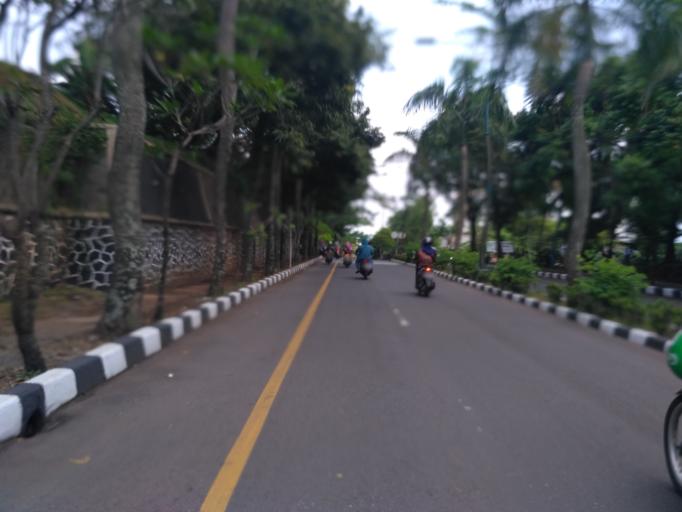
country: ID
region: Central Java
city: Semarang
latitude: -7.0531
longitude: 110.4398
